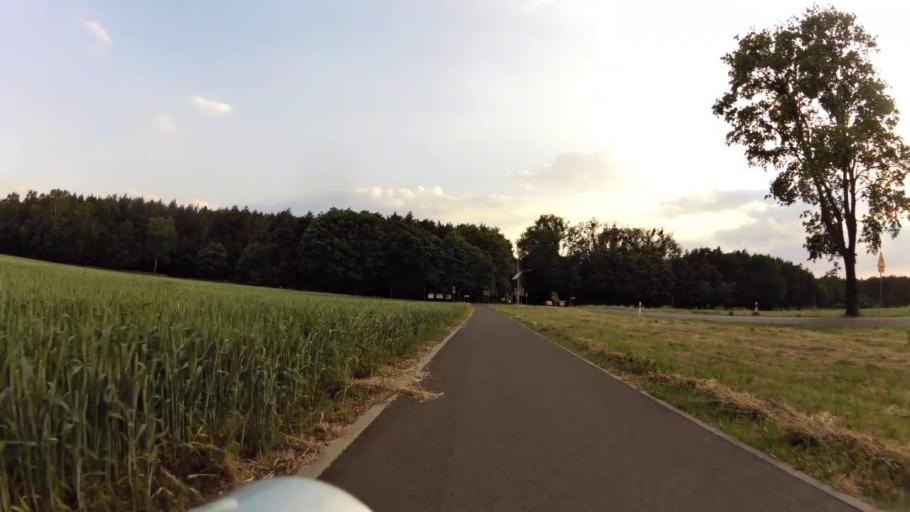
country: PL
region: Kujawsko-Pomorskie
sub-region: Powiat chelminski
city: Unislaw
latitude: 53.1954
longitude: 18.3554
